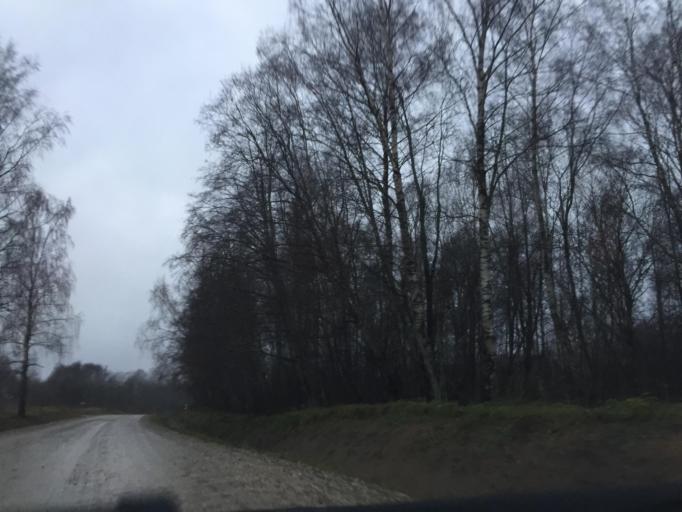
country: LV
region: Salacgrivas
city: Salacgriva
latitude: 57.7648
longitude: 24.4677
